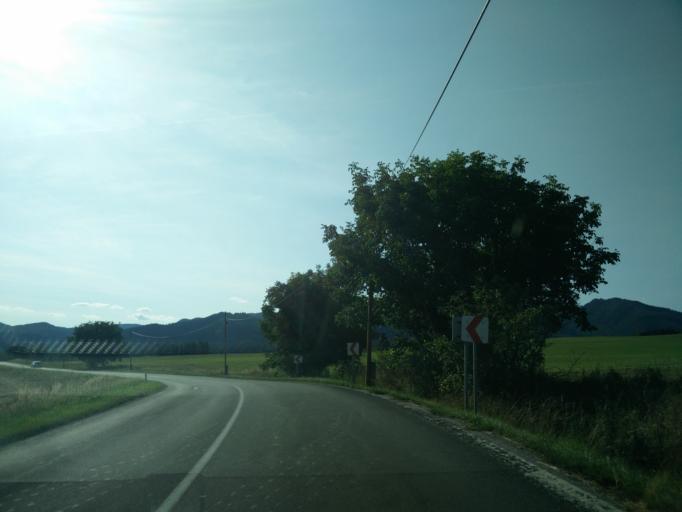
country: SK
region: Zilinsky
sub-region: Okres Martin
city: Martin
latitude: 48.9427
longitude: 18.8178
